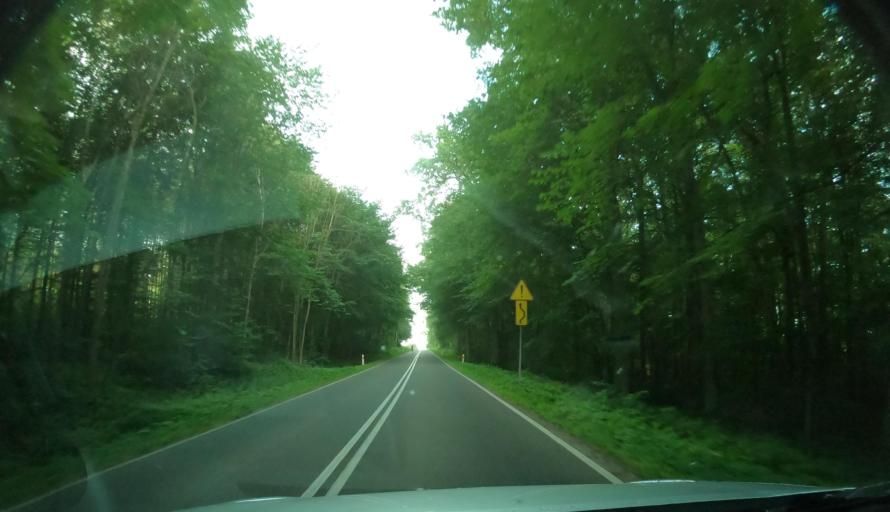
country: PL
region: West Pomeranian Voivodeship
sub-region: Powiat kamienski
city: Golczewo
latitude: 53.8365
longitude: 14.9584
